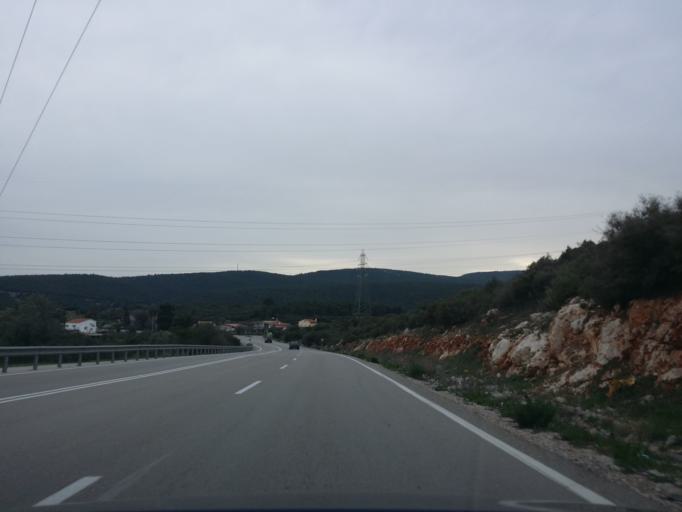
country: GR
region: Attica
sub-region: Nomarchia Dytikis Attikis
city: Vilia
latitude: 38.1538
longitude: 23.4298
